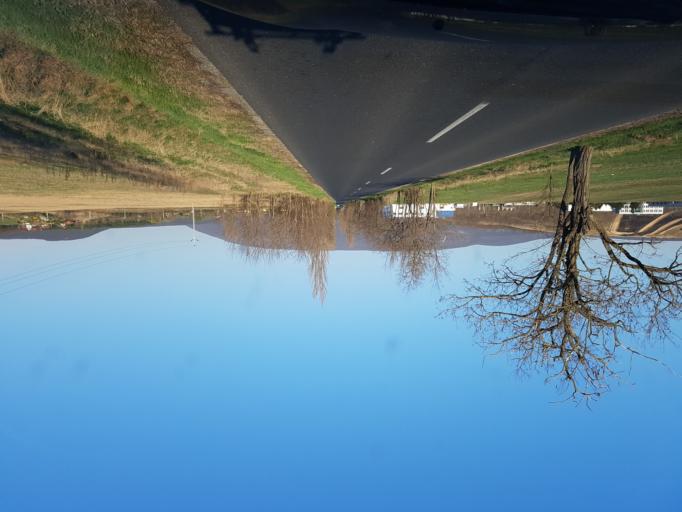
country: HU
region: Komarom-Esztergom
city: Piliscsev
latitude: 47.6717
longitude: 18.7838
